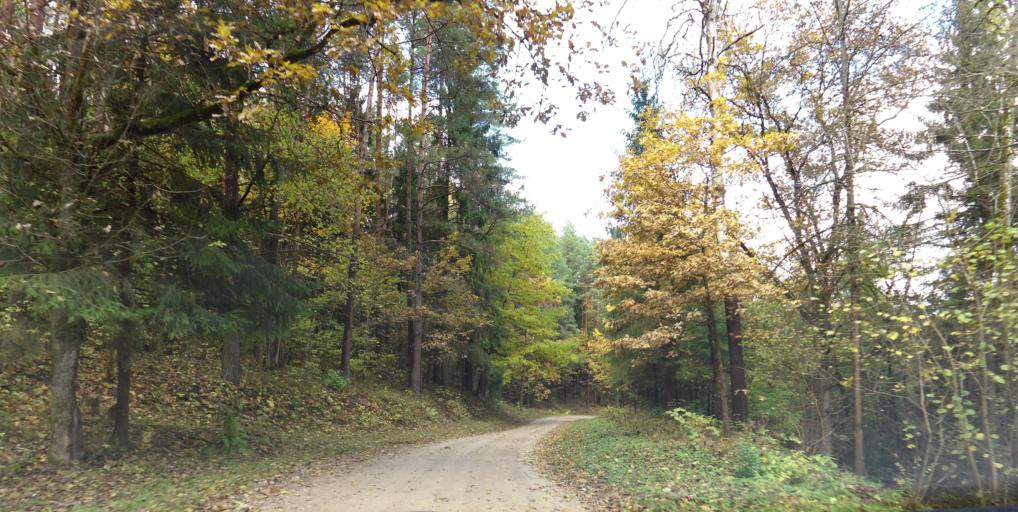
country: LT
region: Vilnius County
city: Vilkpede
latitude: 54.6505
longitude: 25.2523
